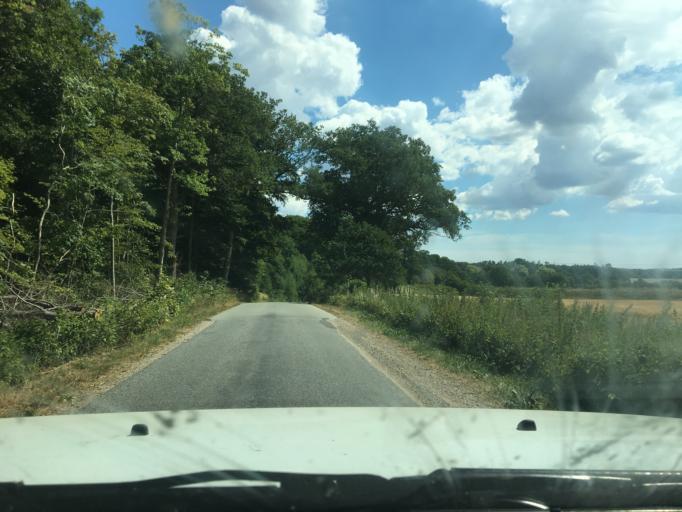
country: DK
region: Central Jutland
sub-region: Syddjurs Kommune
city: Hornslet
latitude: 56.3350
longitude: 10.3215
